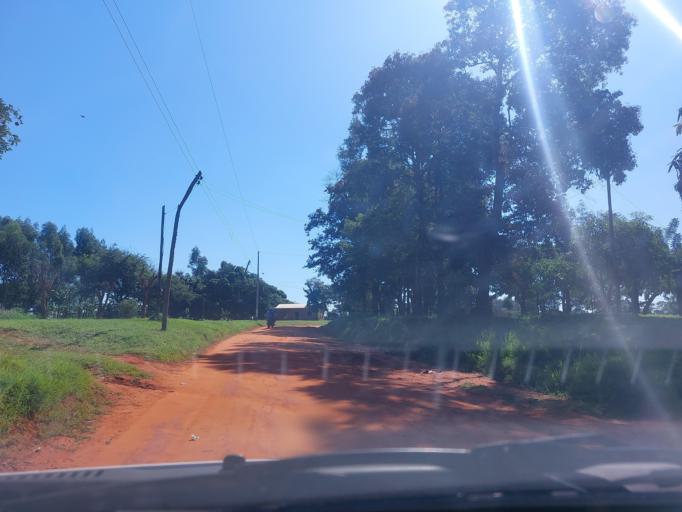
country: PY
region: San Pedro
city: Lima
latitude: -24.1629
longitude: -56.0134
